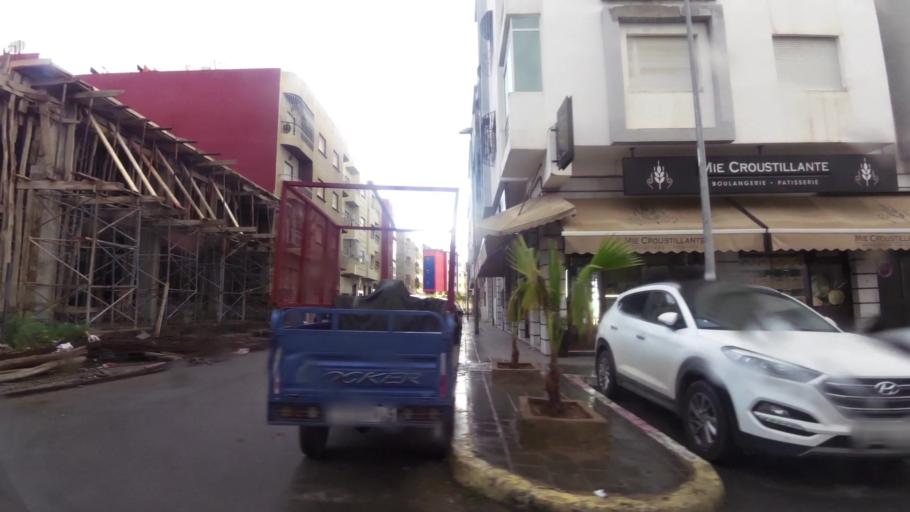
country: MA
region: Grand Casablanca
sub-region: Casablanca
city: Casablanca
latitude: 33.5374
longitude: -7.6718
